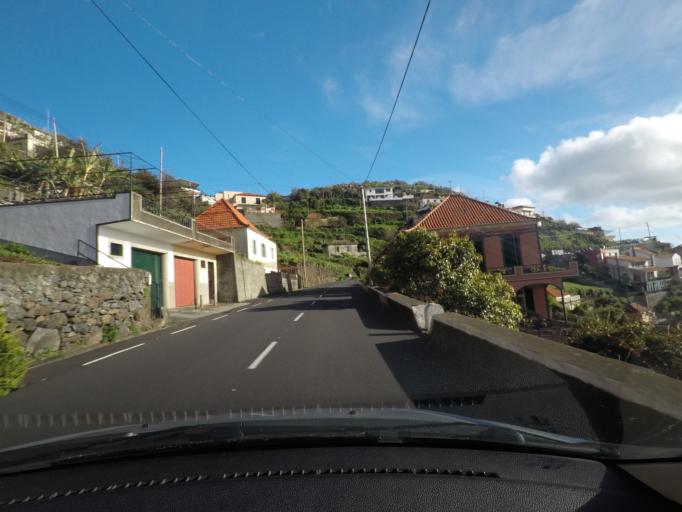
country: PT
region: Madeira
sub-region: Ribeira Brava
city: Campanario
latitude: 32.6690
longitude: -17.0377
